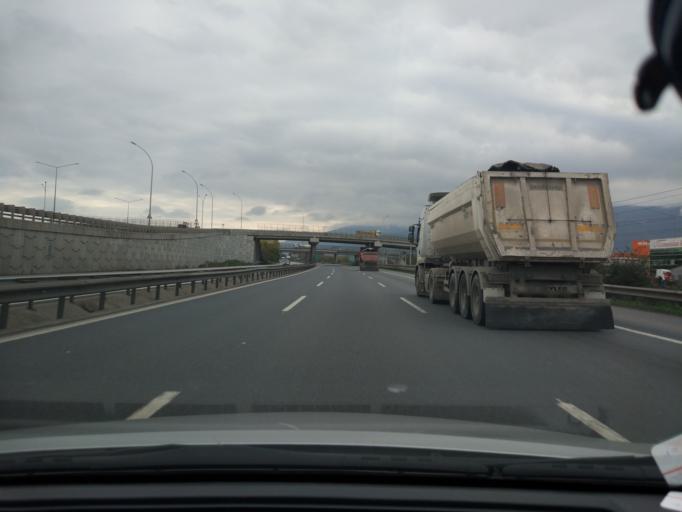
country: TR
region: Kocaeli
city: Derbent
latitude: 40.7329
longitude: 30.0549
